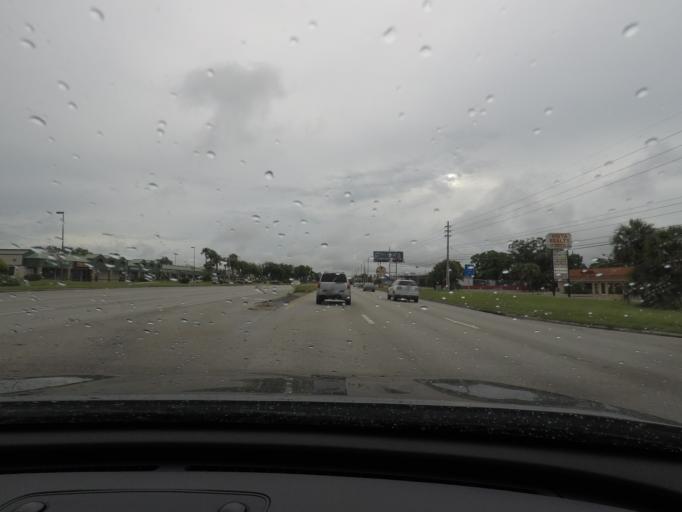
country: US
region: Florida
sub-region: Orange County
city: Azalea Park
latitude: 28.5534
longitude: -81.3236
